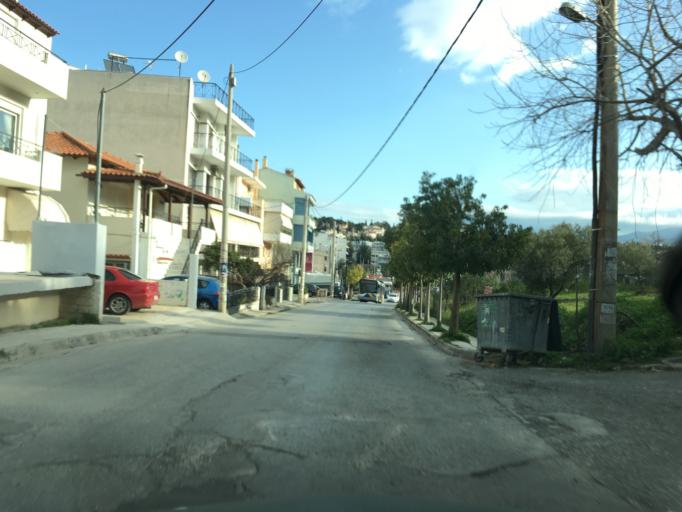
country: GR
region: Attica
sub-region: Nomarchia Athinas
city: Irakleio
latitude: 38.0536
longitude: 23.7755
